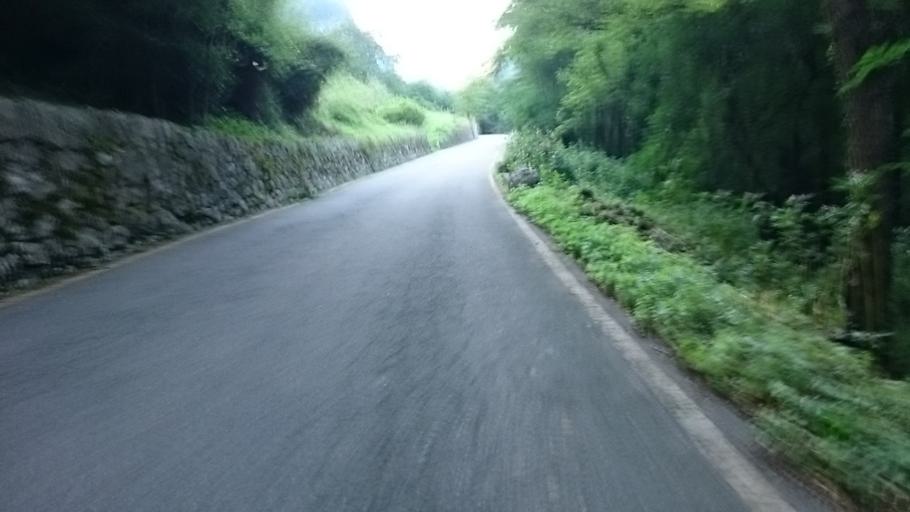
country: IT
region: Veneto
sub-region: Provincia di Vicenza
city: Cismon del Grappa
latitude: 45.9293
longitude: 11.7240
